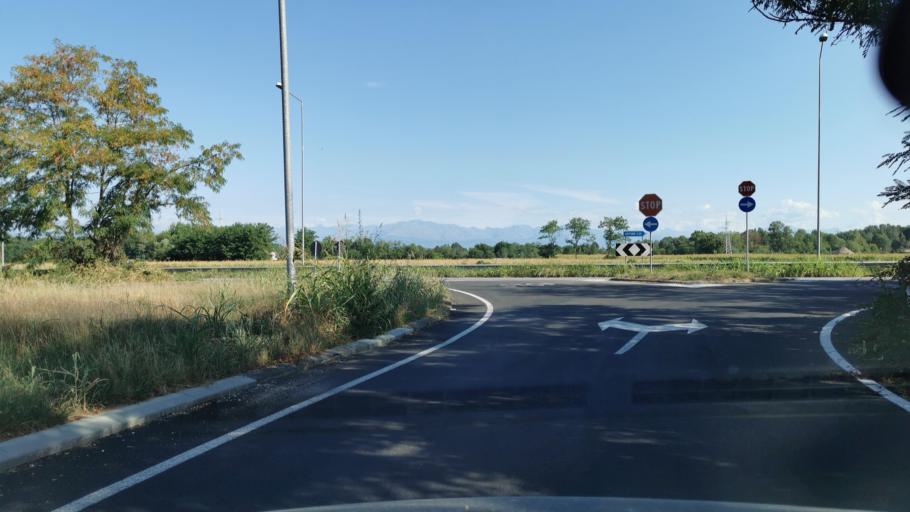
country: IT
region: Piedmont
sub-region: Provincia di Torino
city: Settimo Torinese
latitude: 45.1589
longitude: 7.7787
